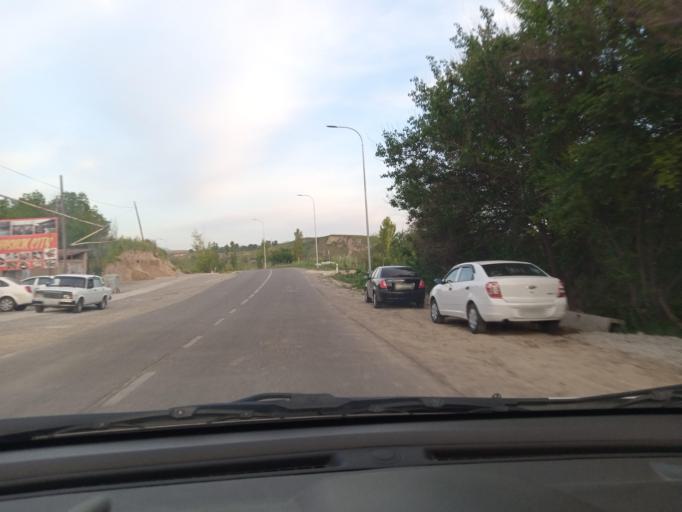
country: UZ
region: Toshkent
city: Parkent
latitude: 41.2460
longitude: 69.7415
